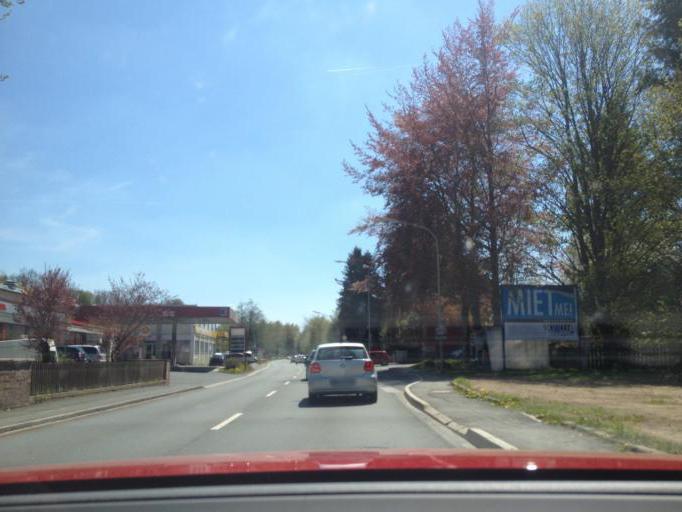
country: DE
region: Bavaria
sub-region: Upper Franconia
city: Oberkotzau
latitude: 50.2599
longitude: 11.9326
